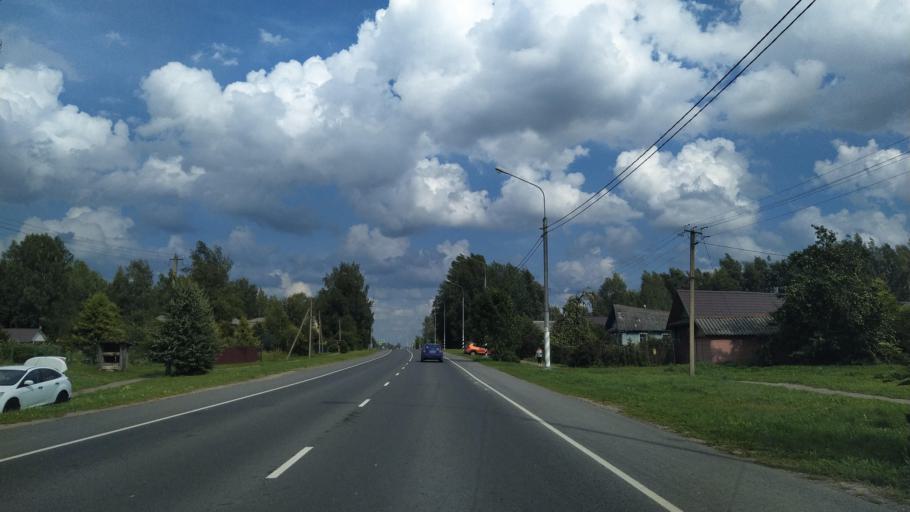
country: RU
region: Novgorod
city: Sol'tsy
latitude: 58.0823
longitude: 30.1071
